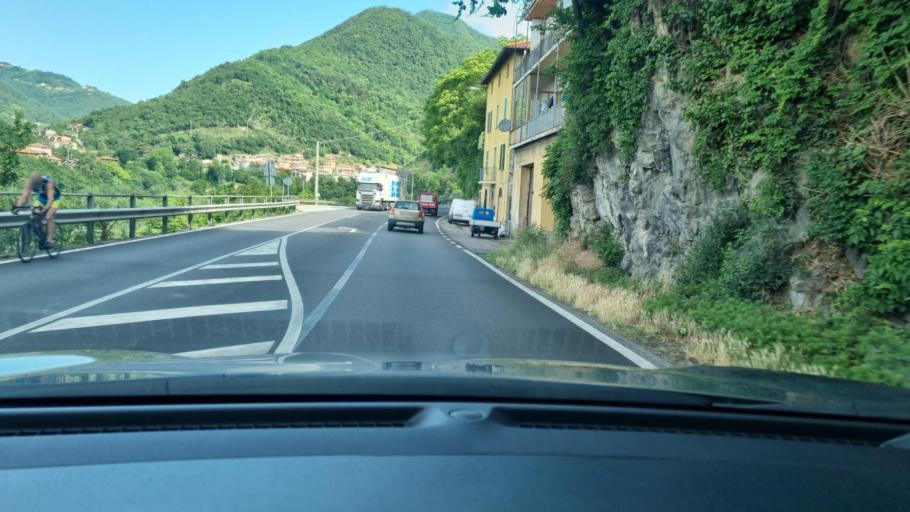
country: IT
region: Lombardy
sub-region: Provincia di Bergamo
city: Villa d'Alme
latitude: 45.7564
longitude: 9.6102
